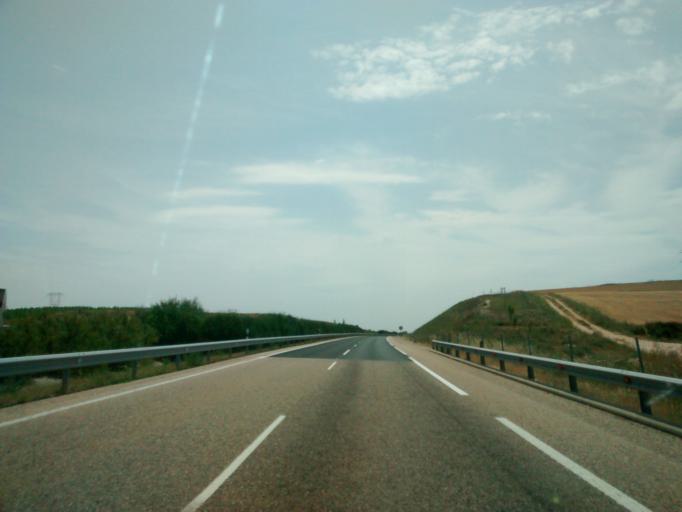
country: ES
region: Castille and Leon
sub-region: Provincia de Burgos
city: Villalbilla de Burgos
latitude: 42.3297
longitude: -3.7750
